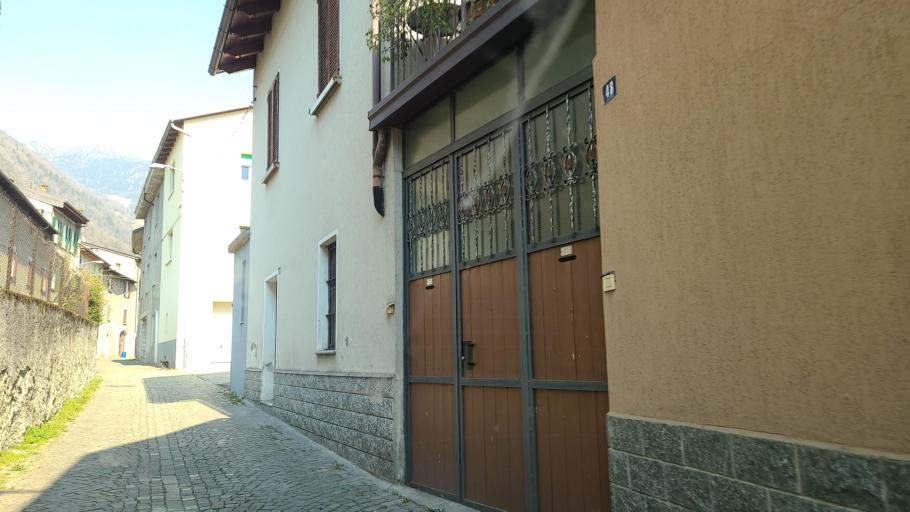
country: IT
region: Lombardy
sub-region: Provincia di Sondrio
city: Tirano
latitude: 46.2199
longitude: 10.1566
